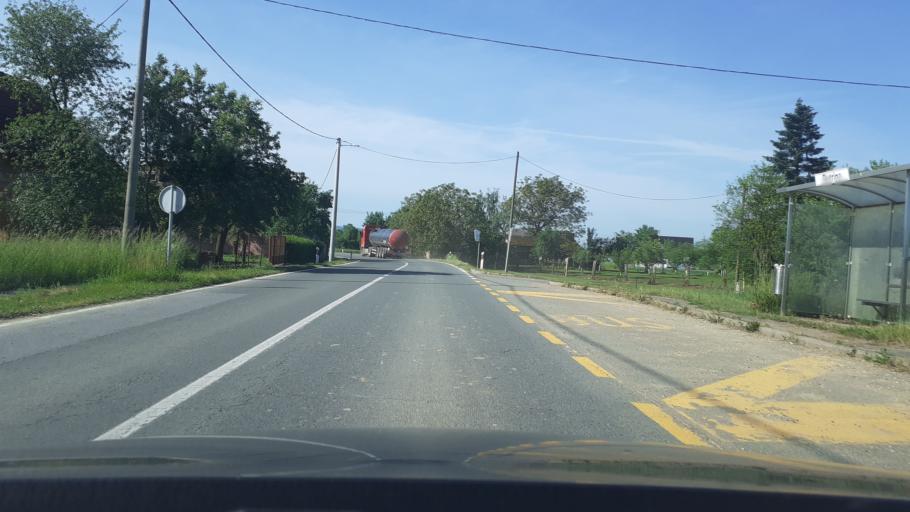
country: HR
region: Brodsko-Posavska
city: Batrina
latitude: 45.1947
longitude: 17.6630
